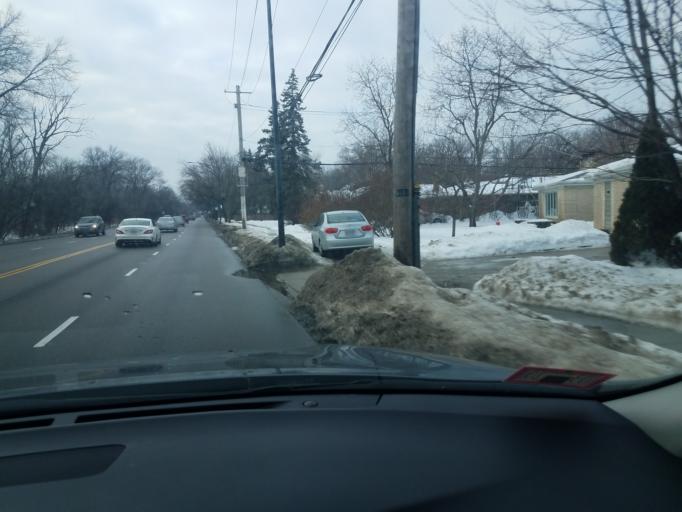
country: US
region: Illinois
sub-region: Cook County
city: Niles
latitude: 42.0024
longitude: -87.7774
